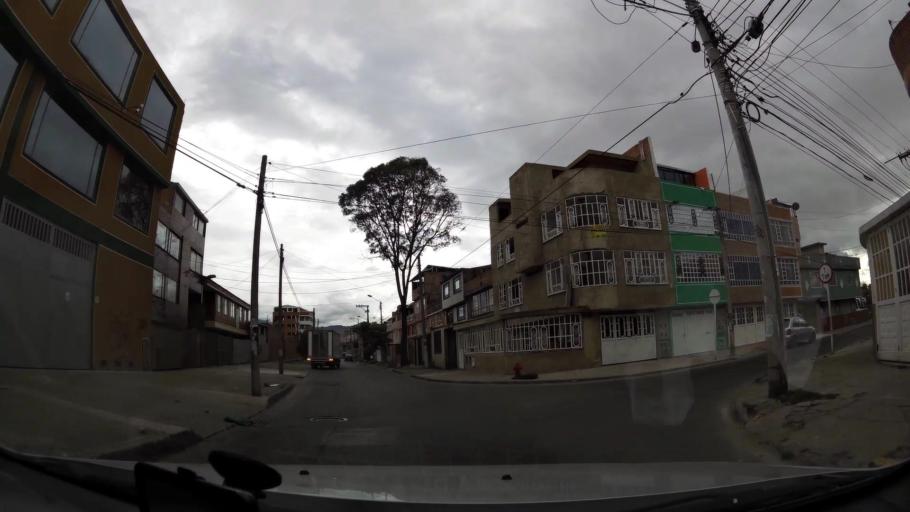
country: CO
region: Bogota D.C.
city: Bogota
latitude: 4.6001
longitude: -74.1420
